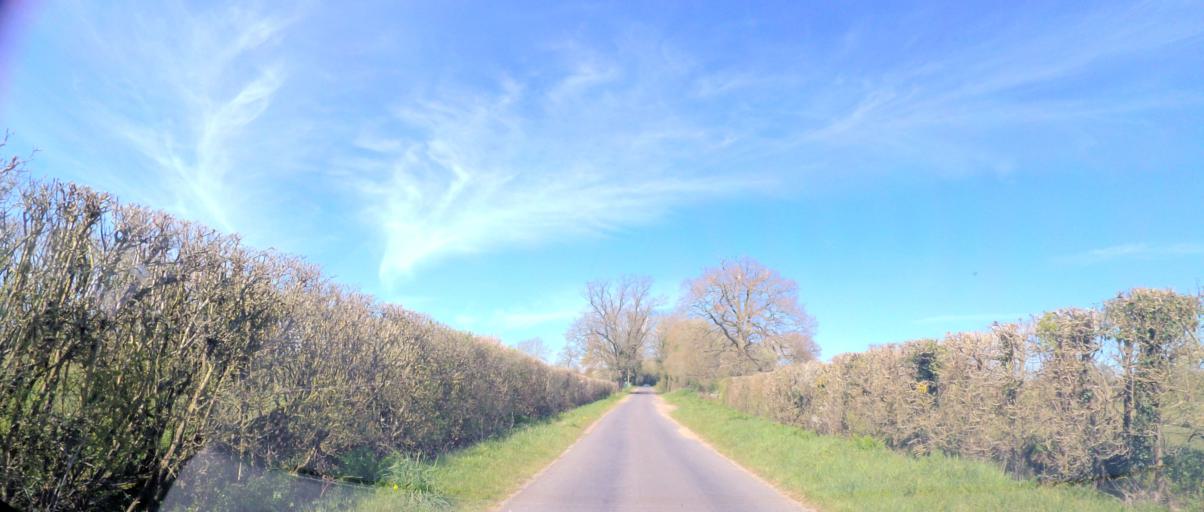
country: GB
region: England
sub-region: West Berkshire
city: Stratfield Mortimer
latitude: 51.3839
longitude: -1.0015
